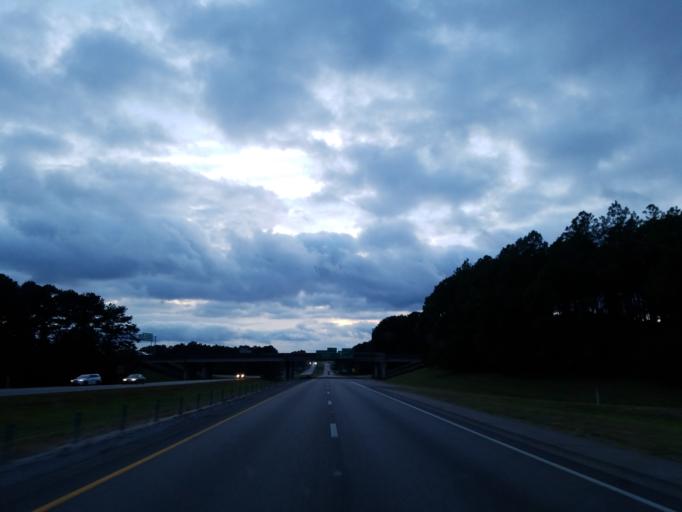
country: US
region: Mississippi
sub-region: Lauderdale County
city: Marion
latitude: 32.3838
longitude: -88.6349
